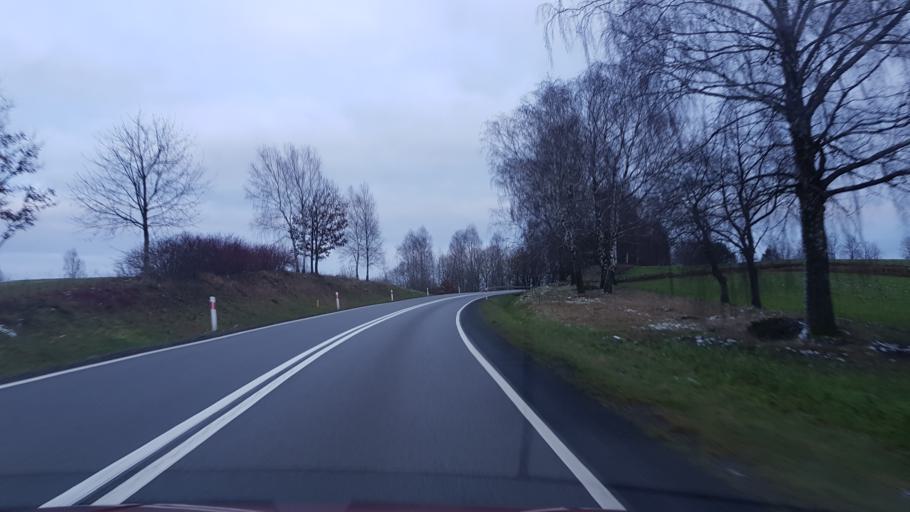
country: PL
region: Pomeranian Voivodeship
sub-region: Powiat bytowski
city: Tuchomie
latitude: 54.0500
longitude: 17.2108
